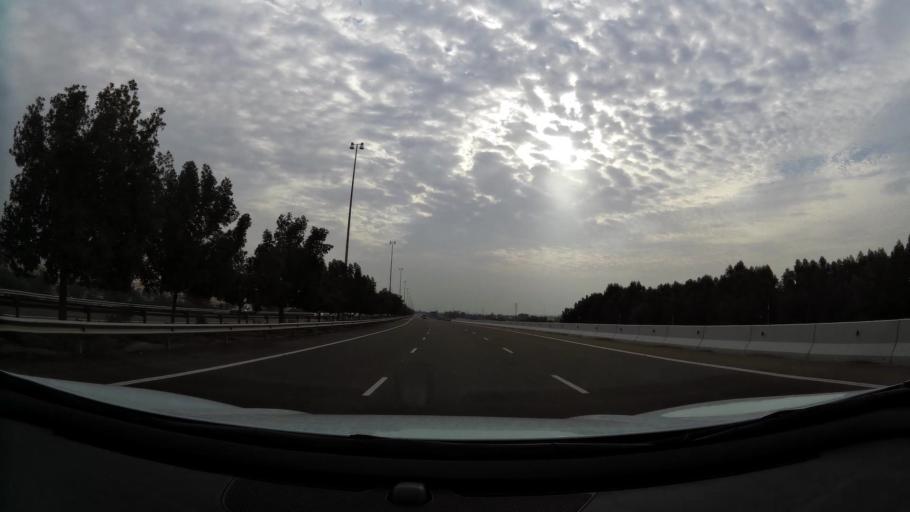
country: AE
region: Abu Dhabi
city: Al Ain
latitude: 24.1810
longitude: 55.0373
